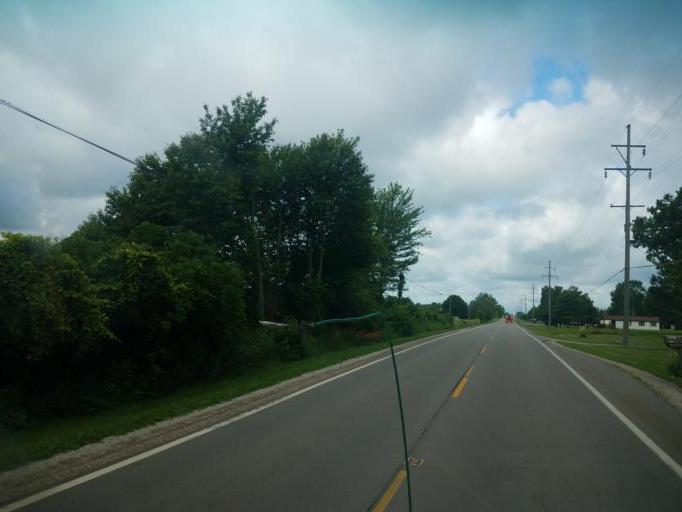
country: US
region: Ohio
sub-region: Marion County
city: Prospect
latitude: 40.4501
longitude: -83.2083
